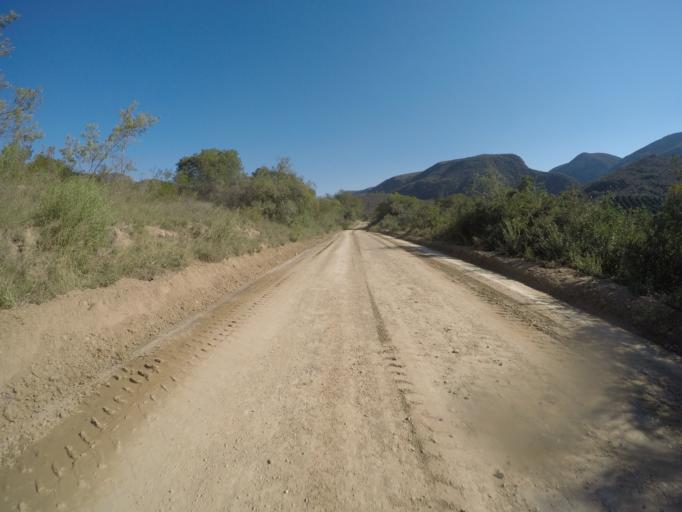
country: ZA
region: Eastern Cape
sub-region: Cacadu District Municipality
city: Kareedouw
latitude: -33.6648
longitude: 24.5431
